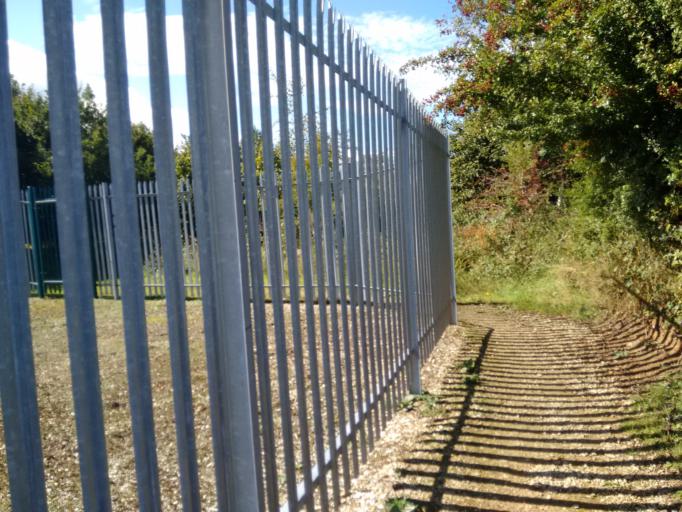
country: GB
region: England
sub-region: Oxfordshire
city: Eynsham
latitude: 51.7767
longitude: -1.3820
